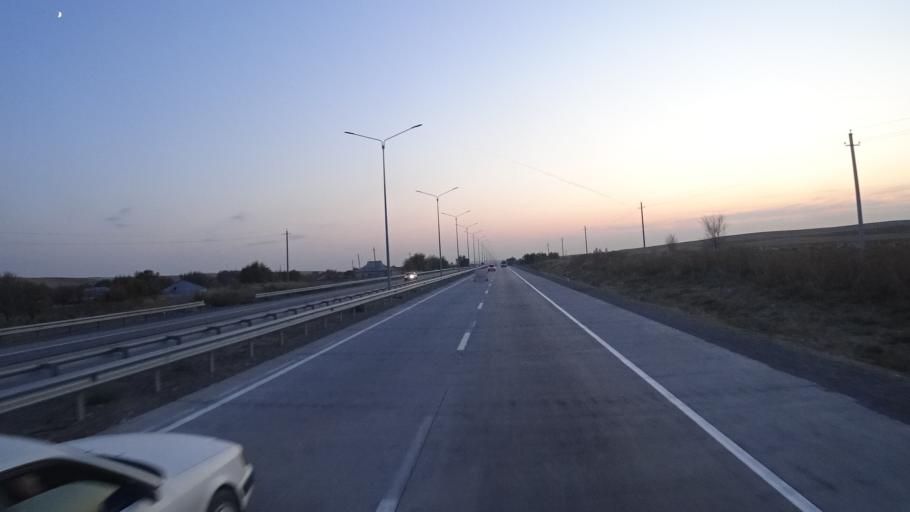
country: KZ
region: Ongtustik Qazaqstan
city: Qazyqurt
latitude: 41.8883
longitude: 69.4448
